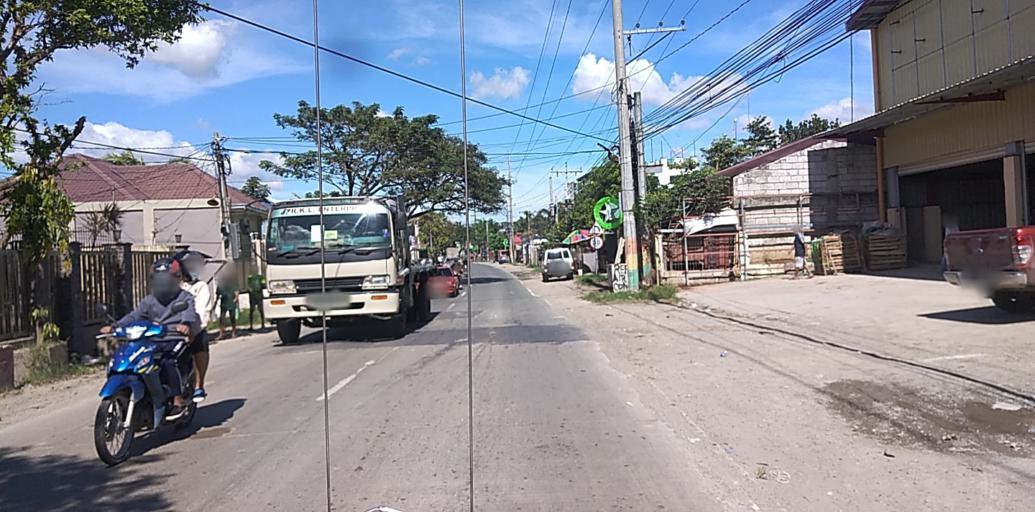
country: PH
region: Central Luzon
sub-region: Province of Pampanga
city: Arayat
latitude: 15.1254
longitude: 120.7758
